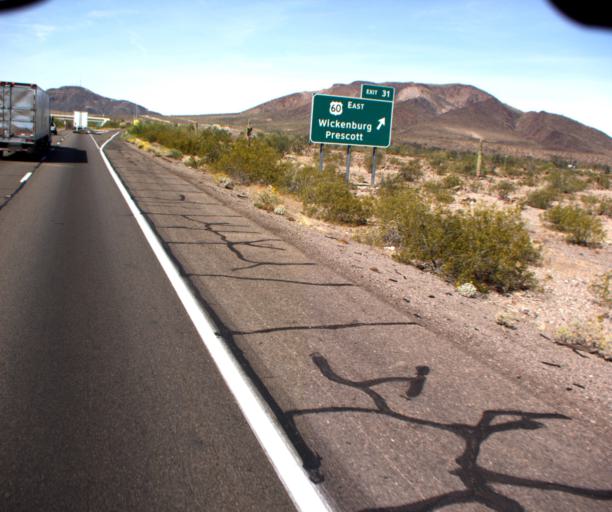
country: US
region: Arizona
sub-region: La Paz County
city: Quartzsite
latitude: 33.6612
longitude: -114.0043
